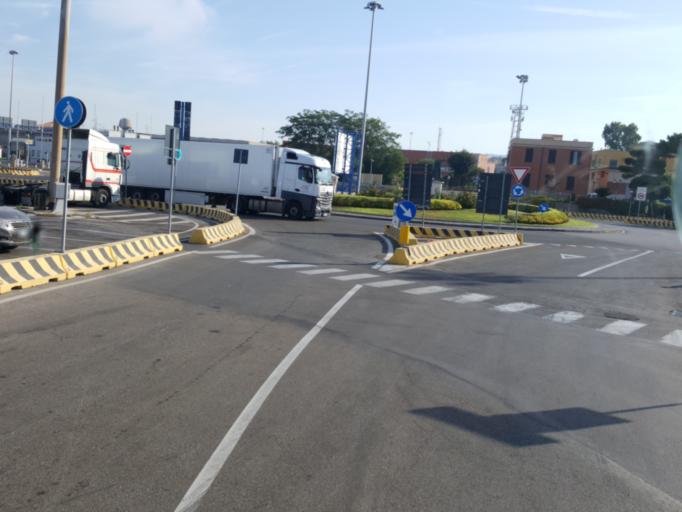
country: IT
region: Latium
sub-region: Citta metropolitana di Roma Capitale
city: Civitavecchia
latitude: 42.0961
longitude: 11.7860
